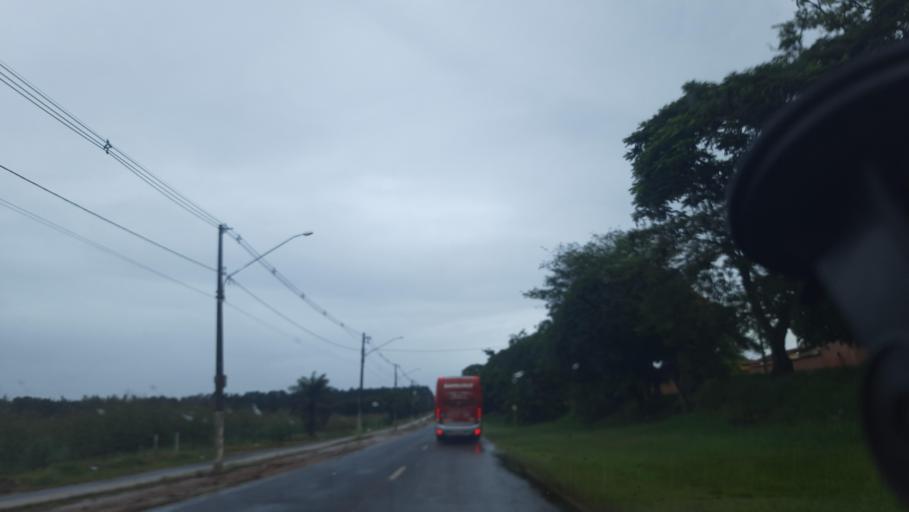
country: BR
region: Sao Paulo
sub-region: Casa Branca
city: Casa Branca
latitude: -21.7773
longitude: -47.0720
